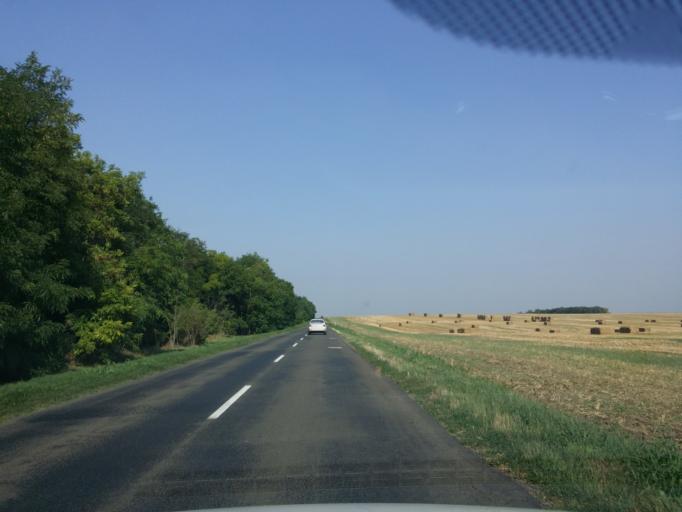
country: HU
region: Fejer
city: Mezofalva
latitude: 46.9389
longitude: 18.7119
